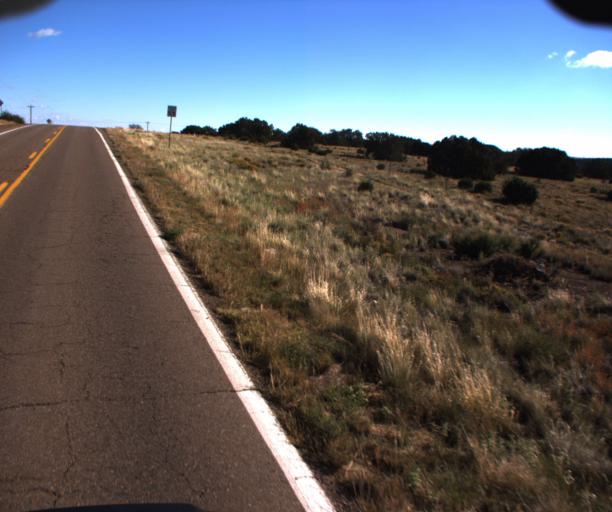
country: US
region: Arizona
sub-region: Apache County
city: Saint Johns
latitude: 34.4539
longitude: -109.6261
